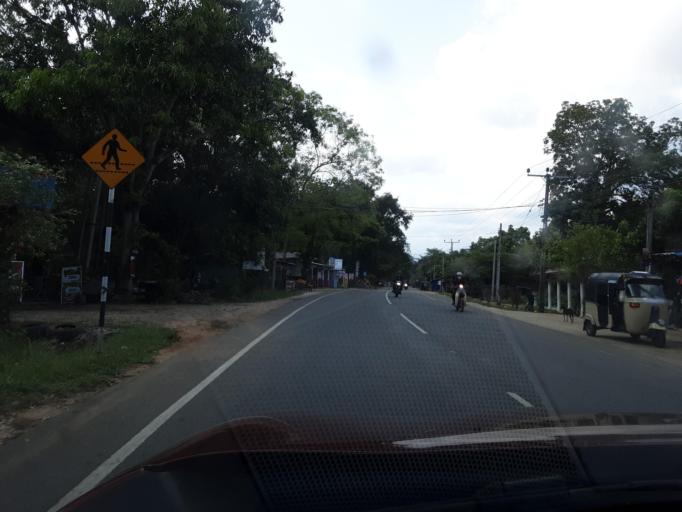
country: LK
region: Uva
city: Haputale
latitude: 6.6867
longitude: 81.1079
